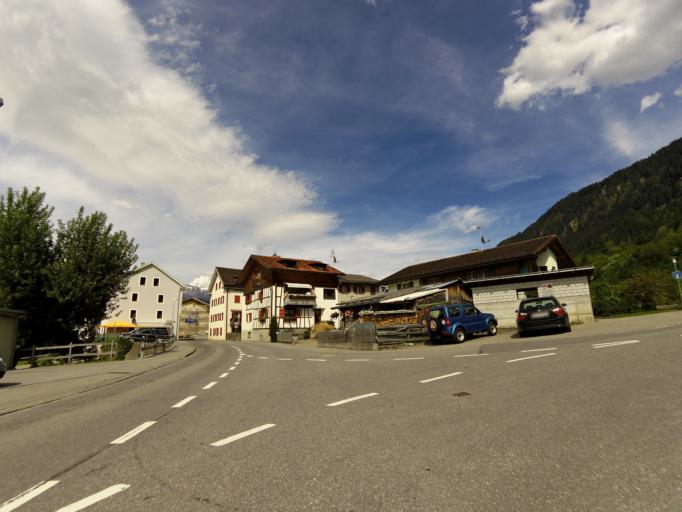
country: CH
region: Grisons
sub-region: Surselva District
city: Ilanz
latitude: 46.7757
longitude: 9.2306
